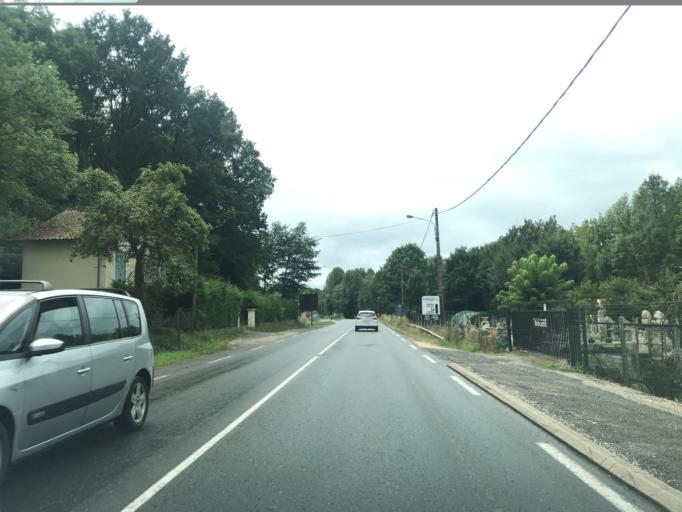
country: FR
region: Aquitaine
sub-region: Departement de la Dordogne
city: Chancelade
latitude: 45.2424
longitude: 0.6863
